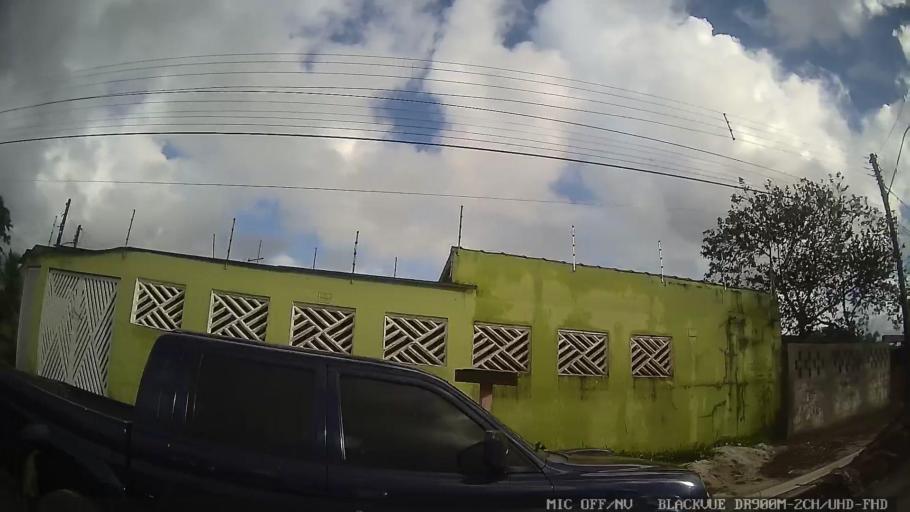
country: BR
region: Sao Paulo
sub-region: Itanhaem
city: Itanhaem
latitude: -24.1715
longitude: -46.8473
